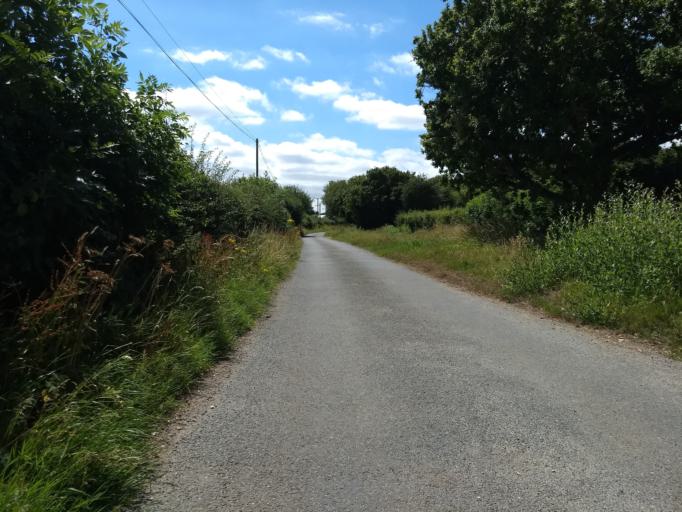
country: GB
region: England
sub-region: Isle of Wight
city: Seaview
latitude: 50.7100
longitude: -1.1357
